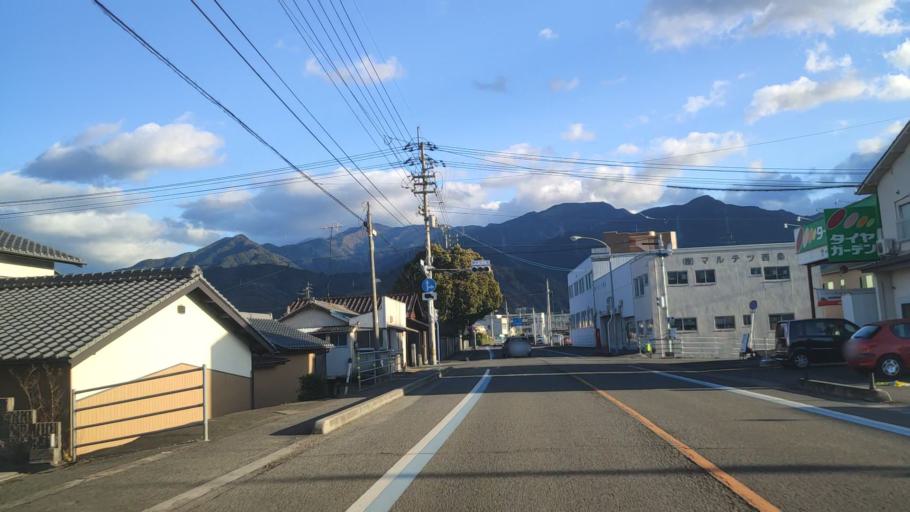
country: JP
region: Ehime
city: Saijo
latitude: 33.9077
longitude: 133.1846
